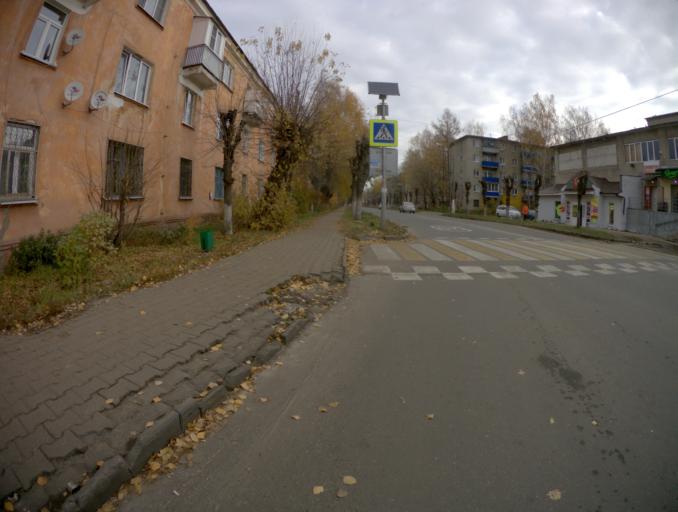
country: RU
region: Moskovskaya
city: Orekhovo-Zuyevo
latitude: 55.7986
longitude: 38.9558
